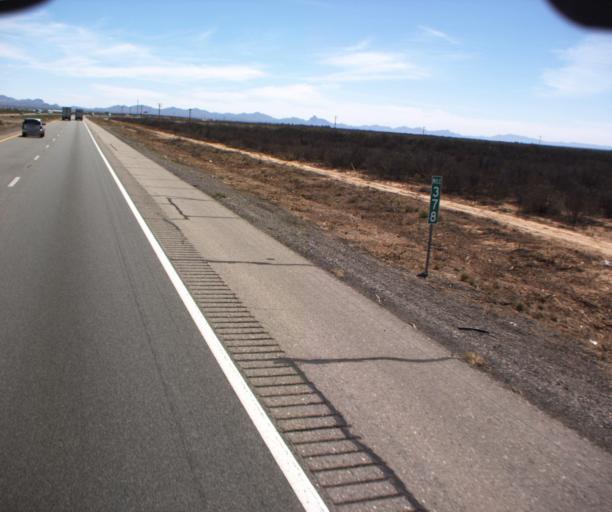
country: US
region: New Mexico
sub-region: Hidalgo County
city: Lordsburg
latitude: 32.2767
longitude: -109.2649
